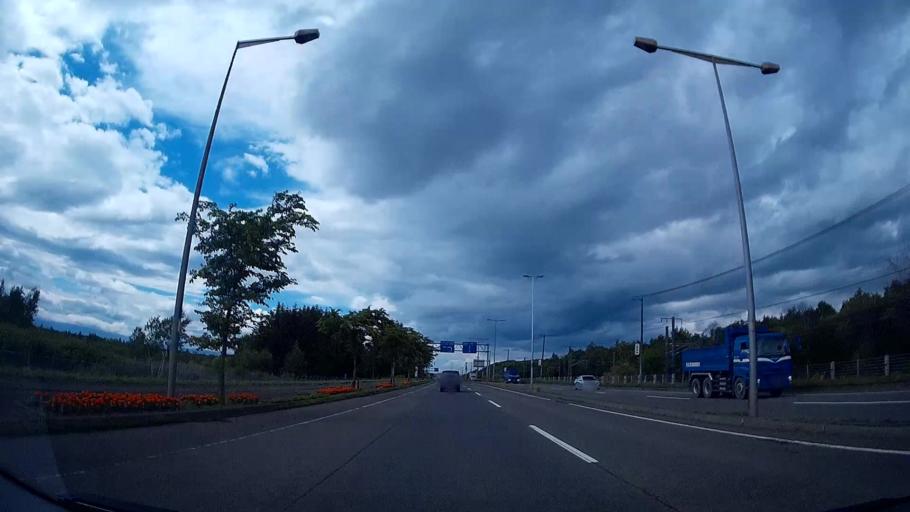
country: JP
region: Hokkaido
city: Chitose
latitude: 42.8139
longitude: 141.6679
